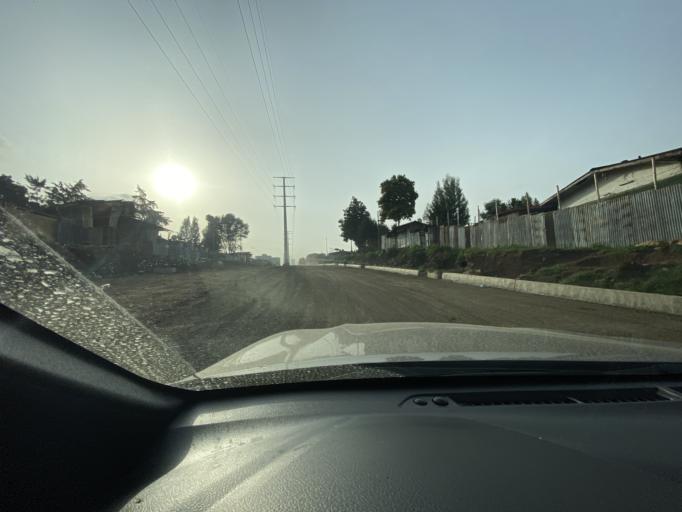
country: ET
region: Adis Abeba
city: Addis Ababa
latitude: 9.0164
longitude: 38.7308
